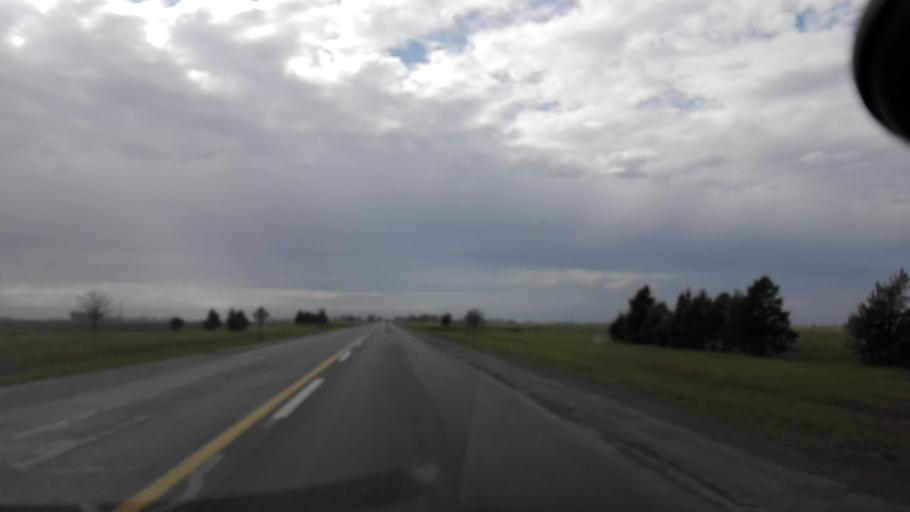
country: AR
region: Buenos Aires
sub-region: Partido de Las Flores
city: Las Flores
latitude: -35.9800
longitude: -59.0409
